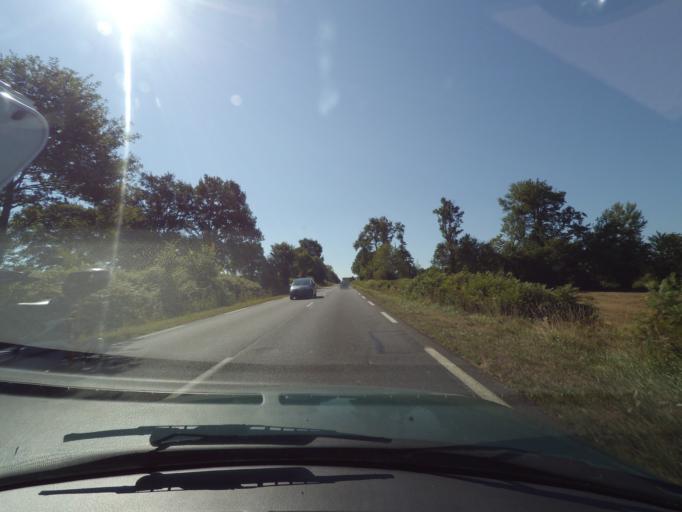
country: FR
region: Limousin
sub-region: Departement de la Haute-Vienne
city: Bussiere-Poitevine
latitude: 46.1931
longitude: 0.9274
